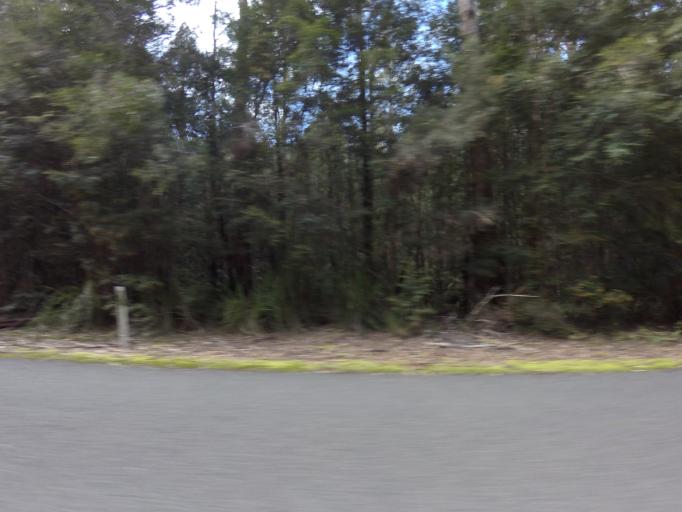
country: AU
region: Tasmania
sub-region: Huon Valley
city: Geeveston
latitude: -42.8200
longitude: 146.3028
